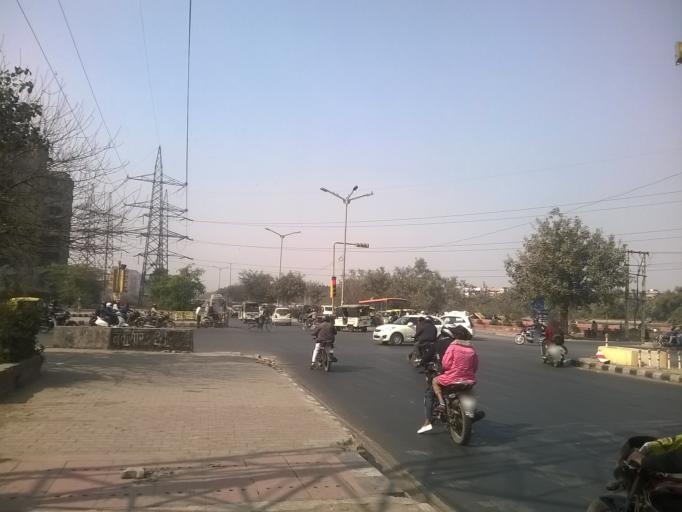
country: IN
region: NCT
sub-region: West Delhi
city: Nangloi Jat
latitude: 28.5981
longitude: 77.0637
